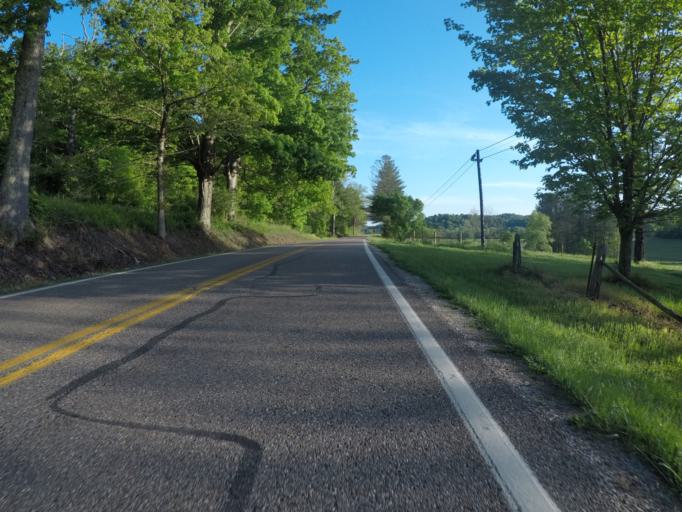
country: US
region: West Virginia
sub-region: Cabell County
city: Huntington
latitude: 38.5481
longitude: -82.4630
